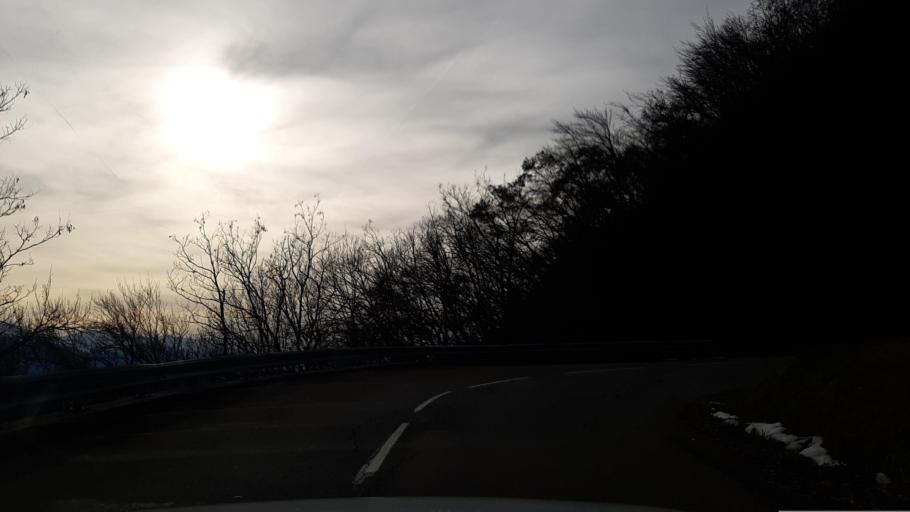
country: FR
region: Rhone-Alpes
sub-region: Departement de la Savoie
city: Coise-Saint-Jean-Pied-Gauthier
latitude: 45.5818
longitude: 6.1437
